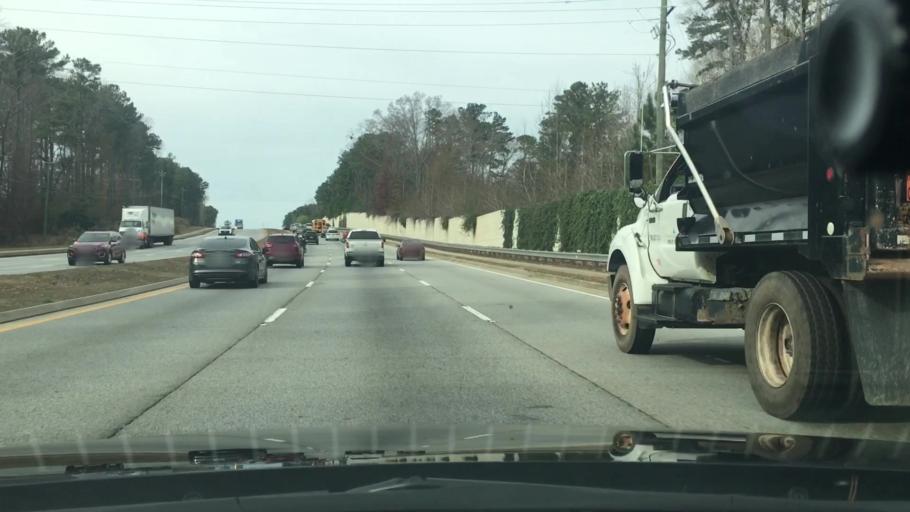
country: US
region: Georgia
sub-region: Fayette County
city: Peachtree City
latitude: 33.3855
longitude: -84.5791
